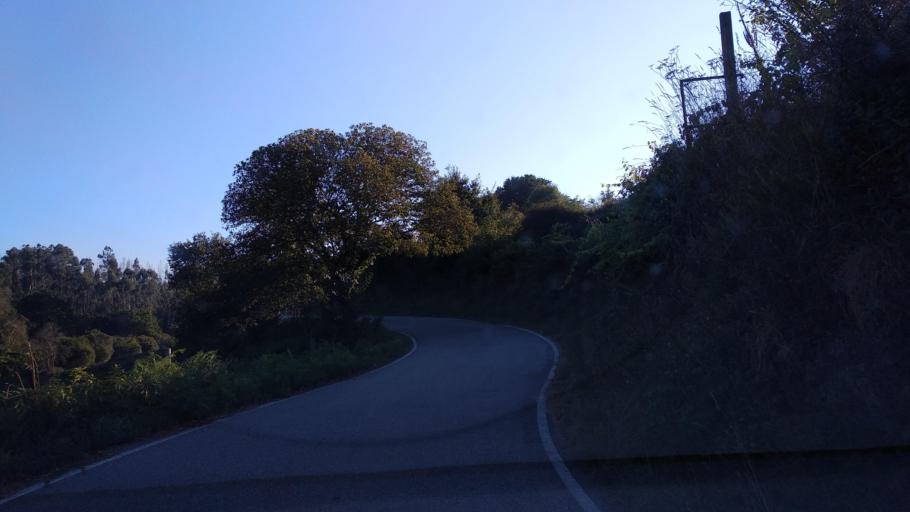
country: ES
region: Galicia
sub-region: Provincia de Pontevedra
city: Ponte Caldelas
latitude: 42.3584
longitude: -8.4931
